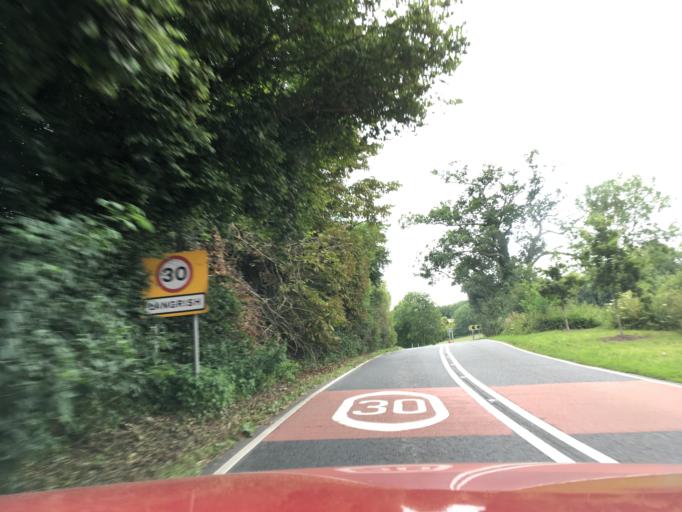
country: GB
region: England
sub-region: Hampshire
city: Petersfield
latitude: 51.0100
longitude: -0.9878
